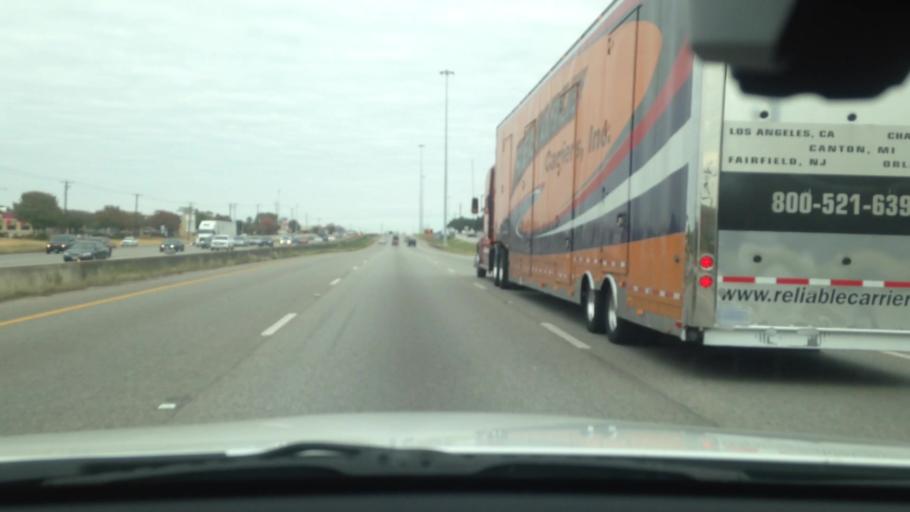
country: US
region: Texas
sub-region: Travis County
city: Onion Creek
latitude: 30.1549
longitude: -97.7909
